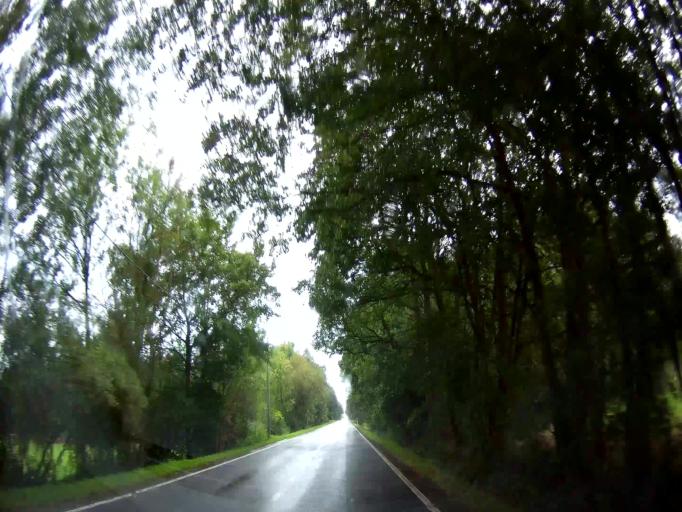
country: BE
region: Wallonia
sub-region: Province de Liege
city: Ferrieres
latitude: 50.4280
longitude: 5.6033
